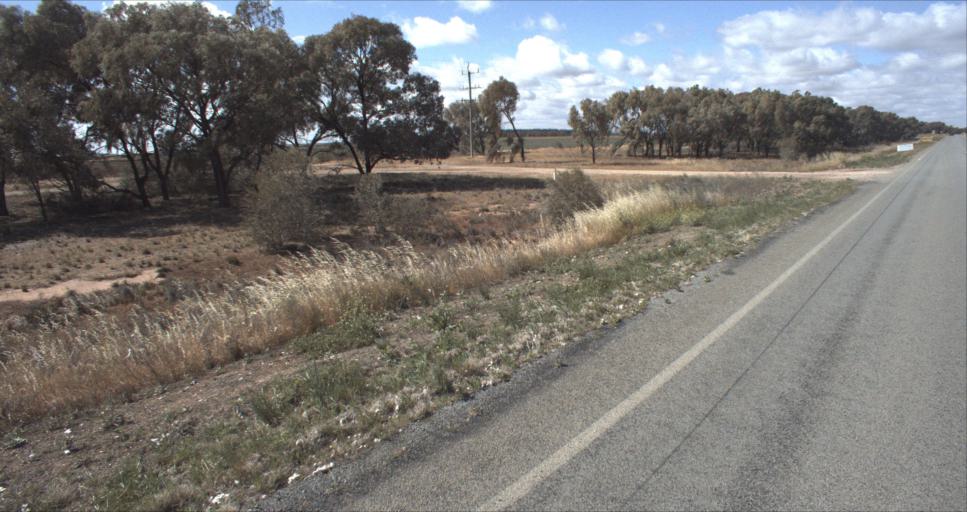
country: AU
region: New South Wales
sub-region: Murrumbidgee Shire
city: Darlington Point
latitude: -34.5484
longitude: 146.1710
